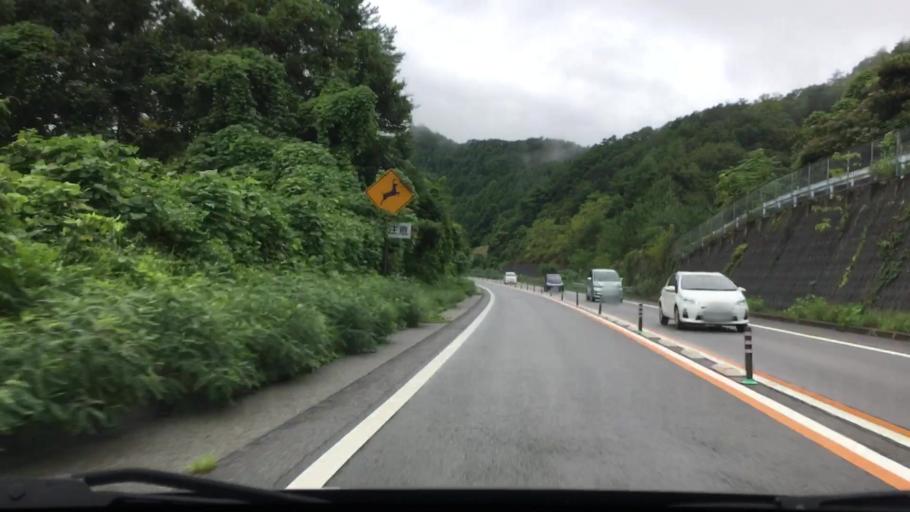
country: JP
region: Hyogo
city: Toyooka
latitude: 35.2602
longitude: 134.7967
